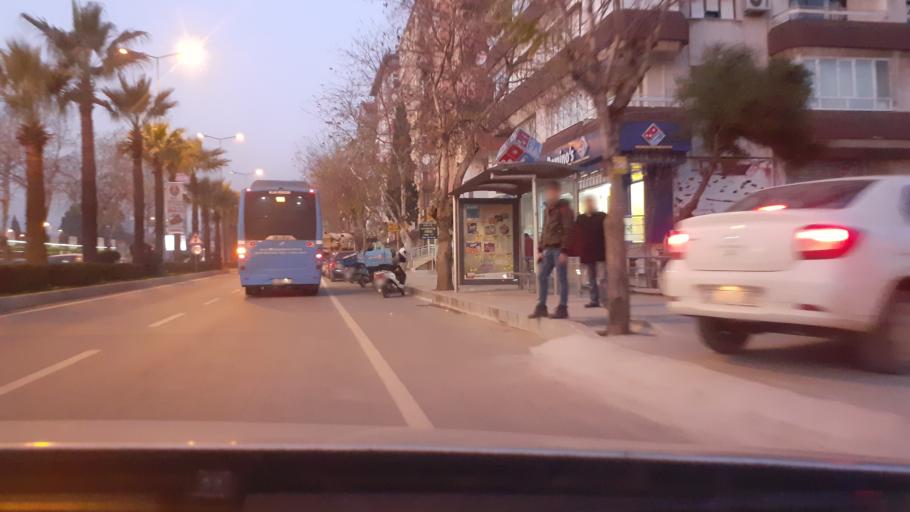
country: TR
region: Hatay
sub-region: Antakya Ilcesi
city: Antakya
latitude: 36.2116
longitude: 36.1599
